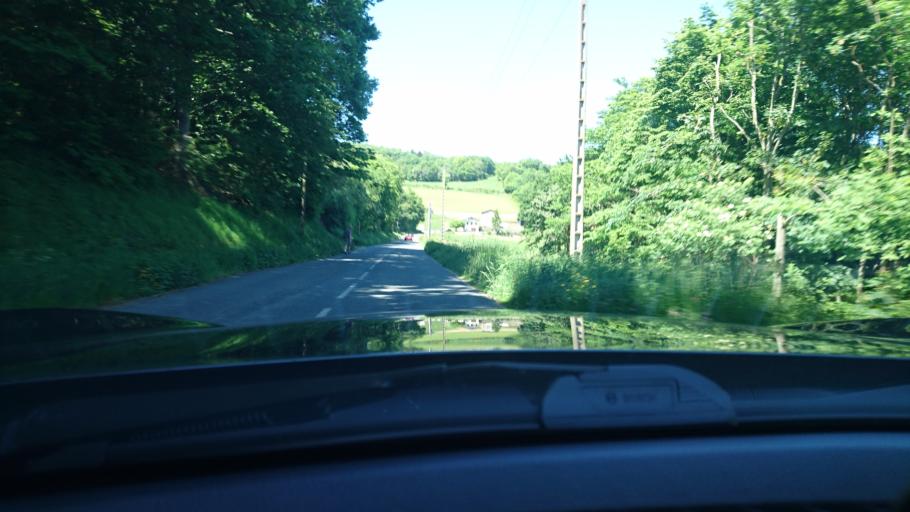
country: FR
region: Rhone-Alpes
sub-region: Departement du Rhone
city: Courzieu
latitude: 45.7139
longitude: 4.5886
